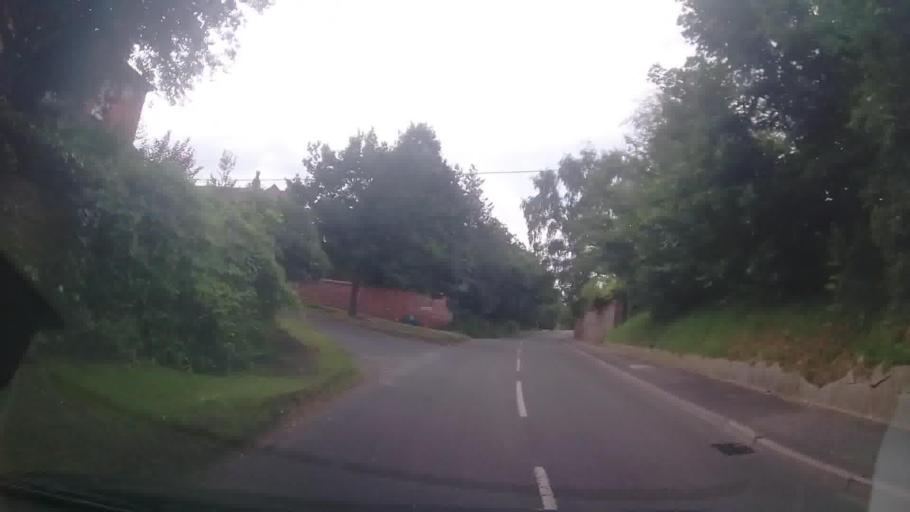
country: GB
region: England
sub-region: Leicestershire
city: Sileby
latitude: 52.7516
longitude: -1.0856
